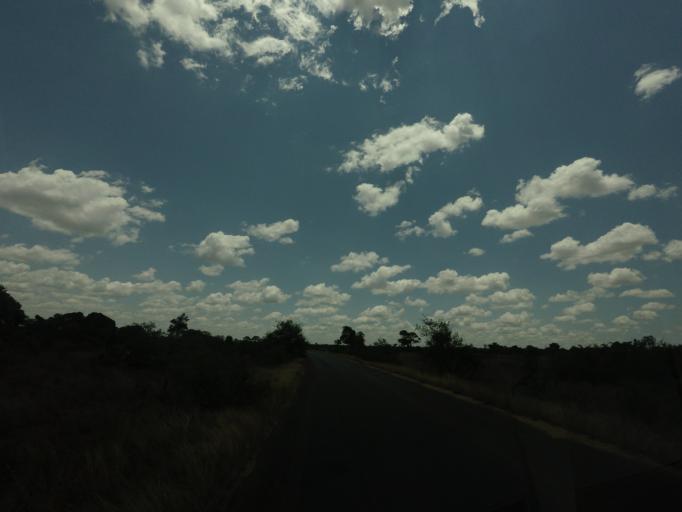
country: ZA
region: Limpopo
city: Thulamahashi
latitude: -24.6795
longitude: 31.8086
